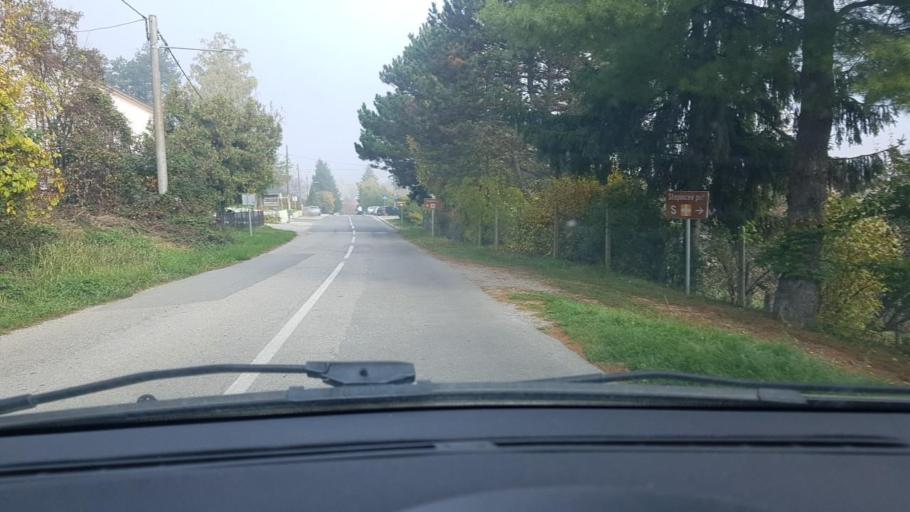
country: HR
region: Krapinsko-Zagorska
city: Zlatar
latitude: 46.1309
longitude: 16.1202
